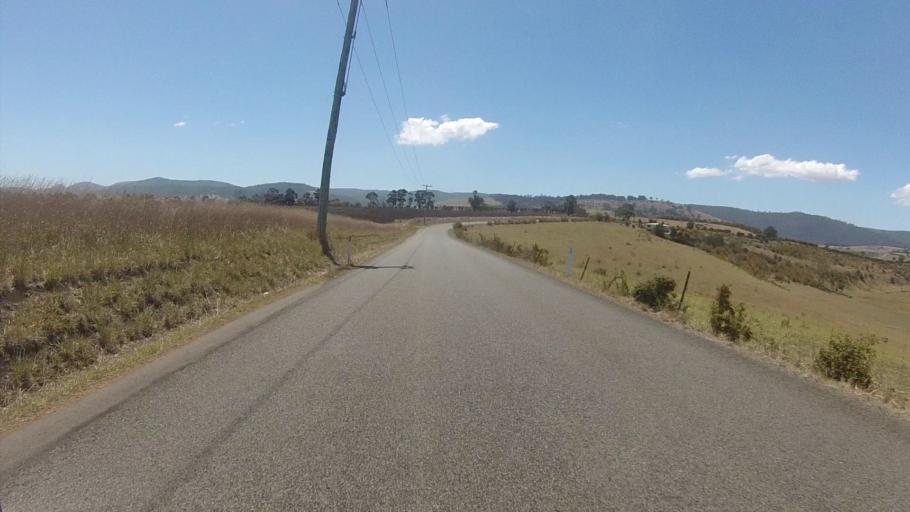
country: AU
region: Tasmania
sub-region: Sorell
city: Sorell
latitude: -42.7770
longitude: 147.5805
